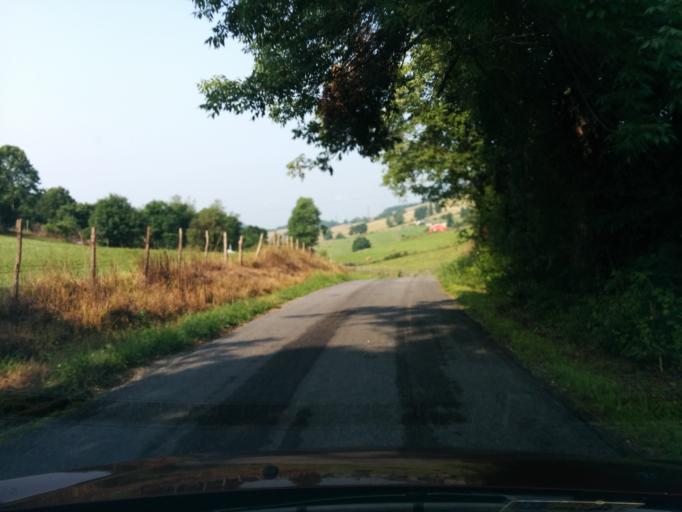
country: US
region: Virginia
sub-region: City of Lexington
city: Lexington
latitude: 37.7889
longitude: -79.5046
